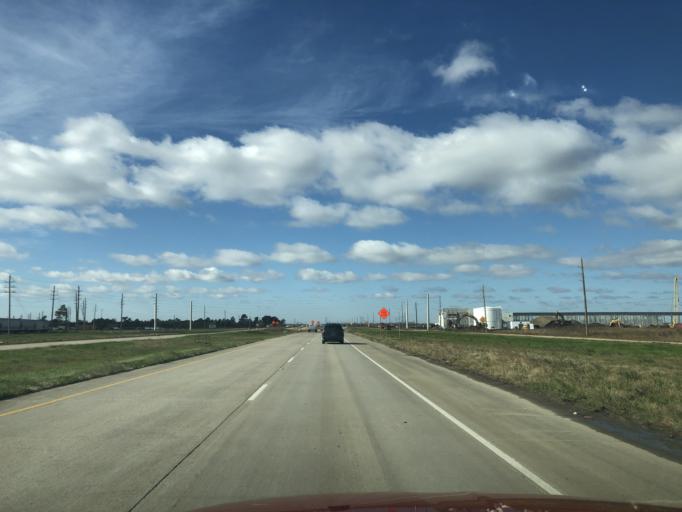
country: US
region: Texas
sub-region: Chambers County
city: Beach City
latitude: 29.7280
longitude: -94.9008
